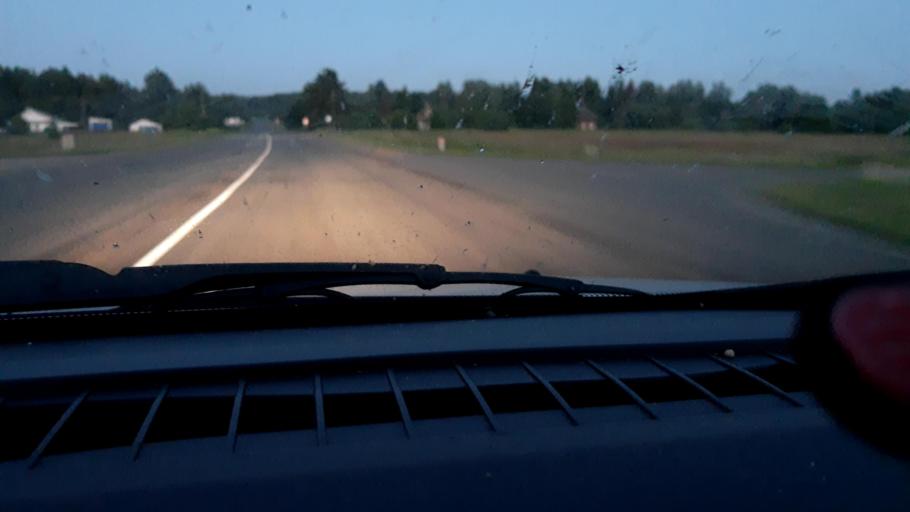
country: RU
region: Nizjnij Novgorod
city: Tonkino
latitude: 57.3537
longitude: 46.4321
